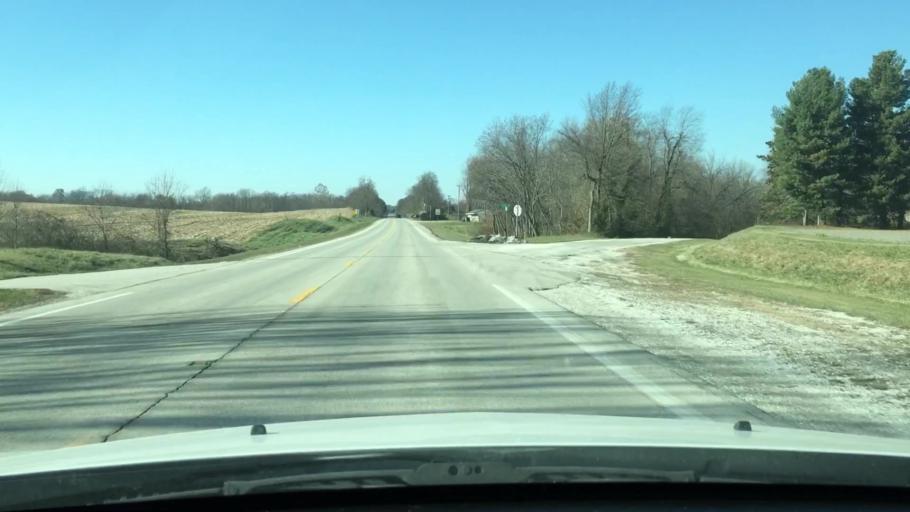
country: US
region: Illinois
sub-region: Pike County
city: Griggsville
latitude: 39.6201
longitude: -90.6815
